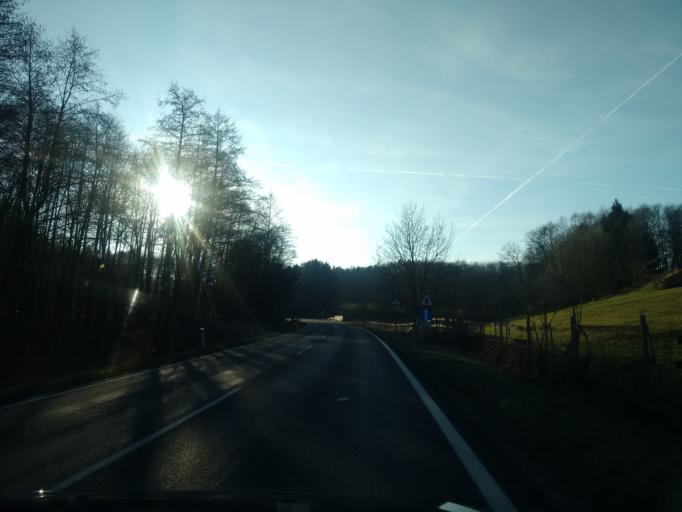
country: AT
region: Lower Austria
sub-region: Politischer Bezirk Sankt Polten
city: Kirchstetten
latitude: 48.1817
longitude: 15.8594
